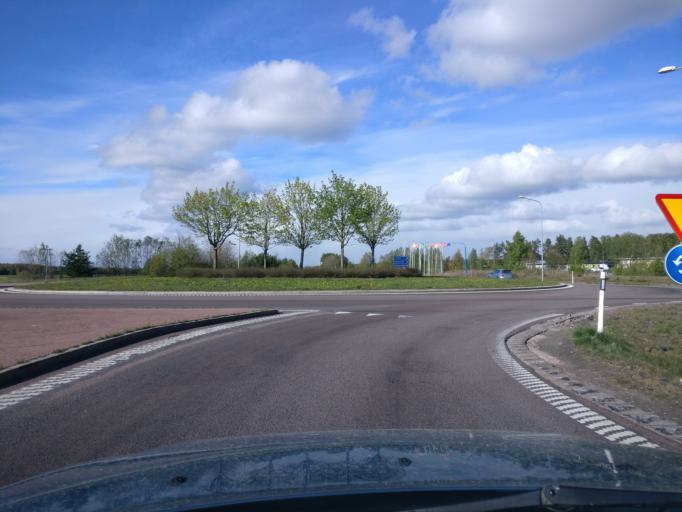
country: SE
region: Vaermland
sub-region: Karlstads Kommun
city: Karlstad
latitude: 59.4289
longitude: 13.4108
